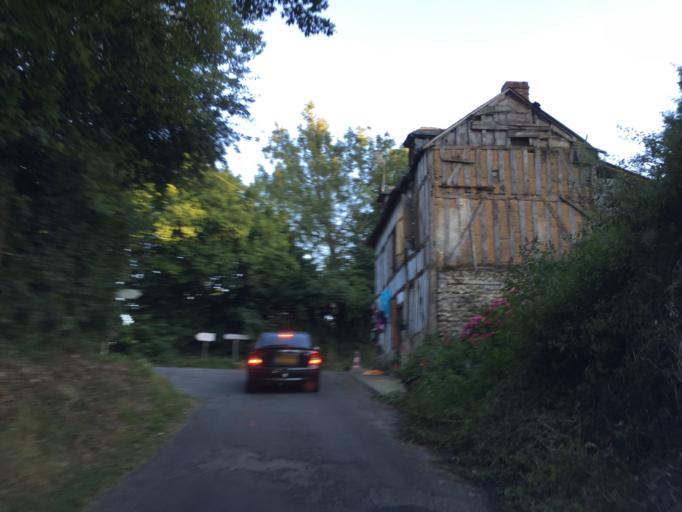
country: FR
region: Lower Normandy
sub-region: Departement du Calvados
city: Equemauville
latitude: 49.4060
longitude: 0.2054
